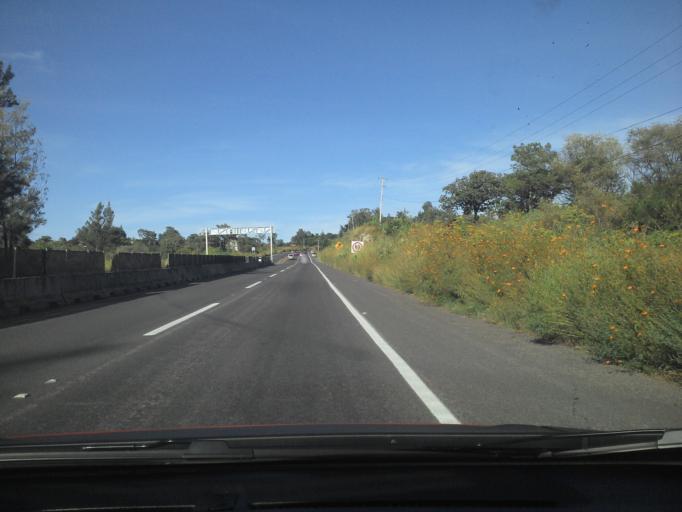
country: MX
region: Jalisco
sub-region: Tala
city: Los Ruisenores
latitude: 20.7242
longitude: -103.6212
